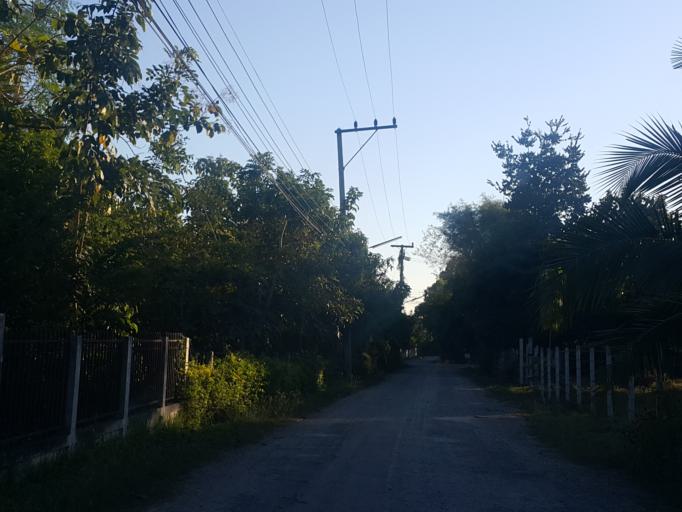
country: TH
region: Chiang Mai
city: San Sai
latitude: 18.8763
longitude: 99.1626
